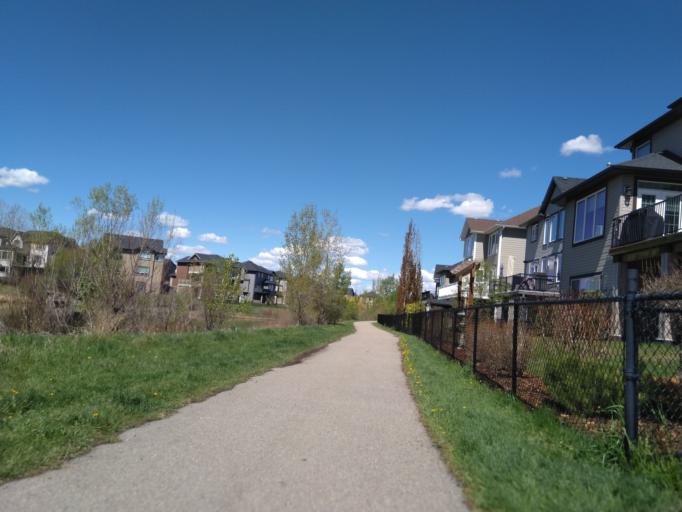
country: CA
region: Alberta
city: Chestermere
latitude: 51.0265
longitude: -113.8332
